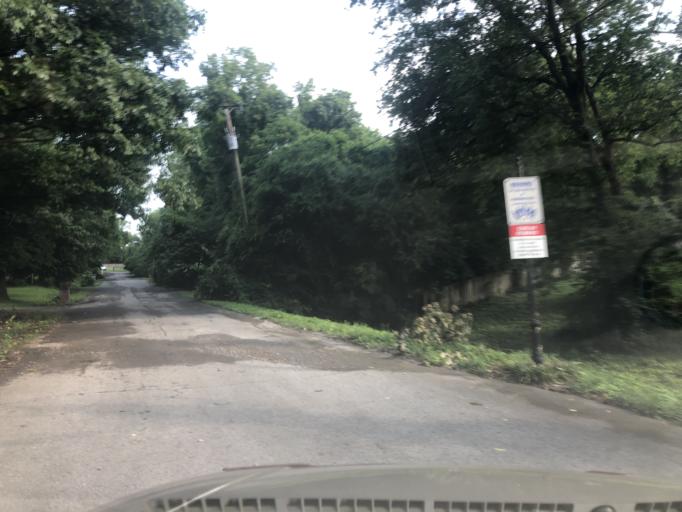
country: US
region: Tennessee
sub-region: Davidson County
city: Lakewood
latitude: 36.2434
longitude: -86.7101
